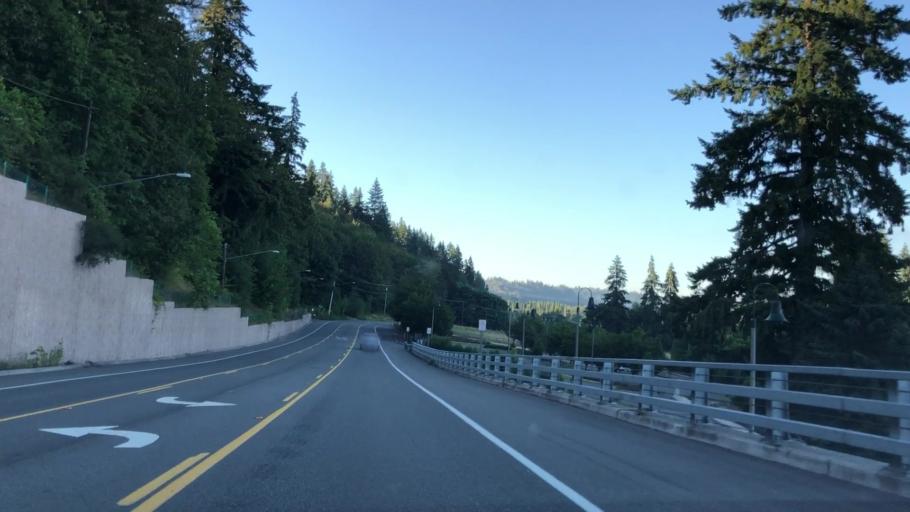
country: US
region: Washington
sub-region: King County
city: Sammamish
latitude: 47.6840
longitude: -122.0803
